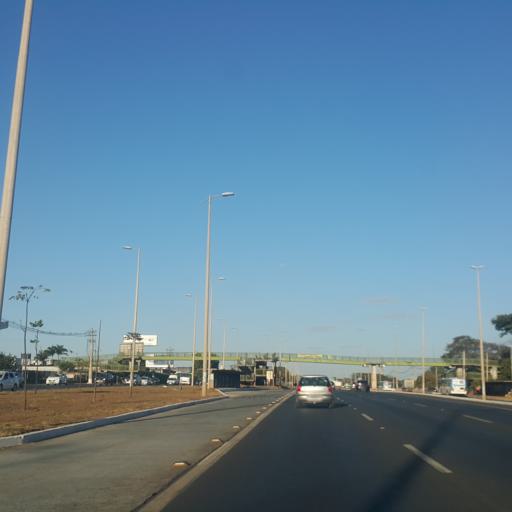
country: BR
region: Federal District
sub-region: Brasilia
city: Brasilia
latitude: -15.8086
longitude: -47.9594
